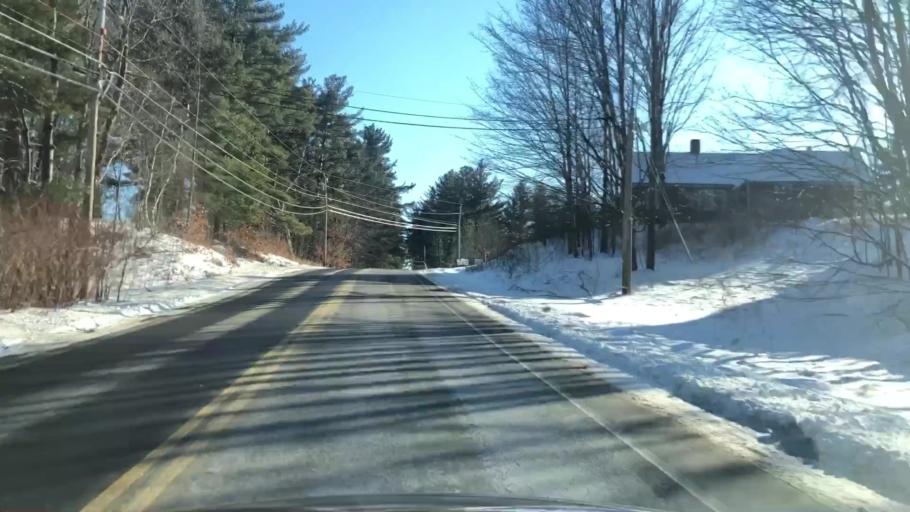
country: US
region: New Hampshire
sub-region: Hillsborough County
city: Wilton
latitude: 42.8366
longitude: -71.7056
